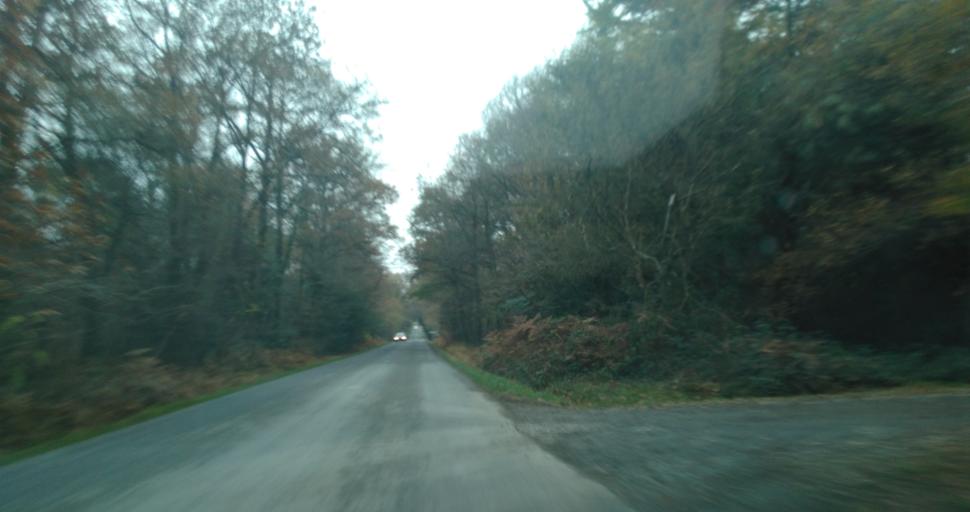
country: FR
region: Brittany
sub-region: Departement d'Ille-et-Vilaine
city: Iffendic
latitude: 48.0988
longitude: -2.0428
